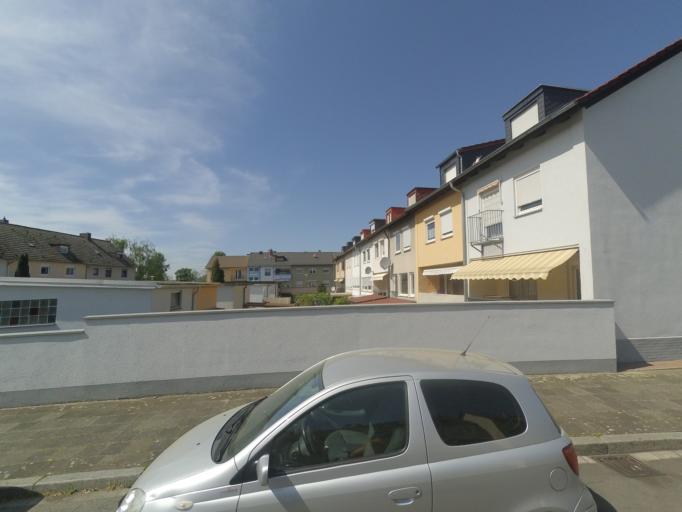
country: DE
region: Rheinland-Pfalz
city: Ludwigshafen am Rhein
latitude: 49.4684
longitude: 8.4304
